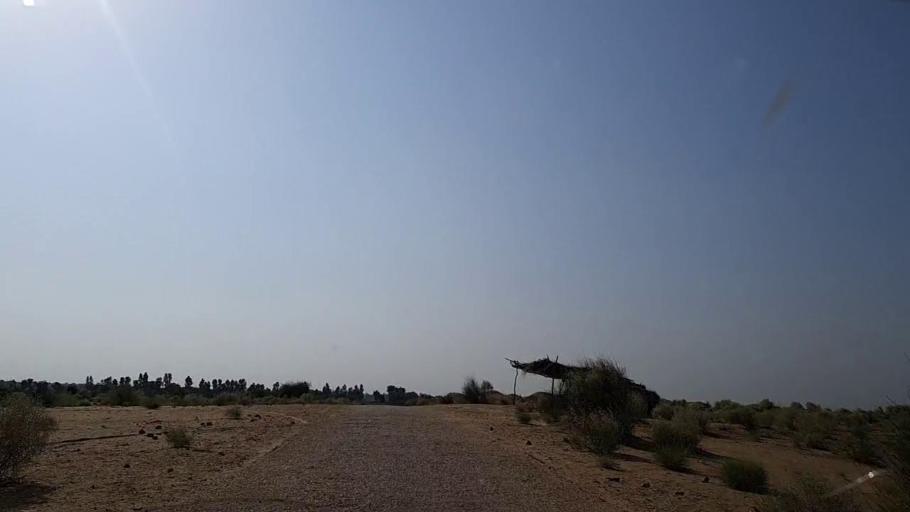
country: PK
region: Sindh
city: Khanpur
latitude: 27.7363
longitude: 69.3739
